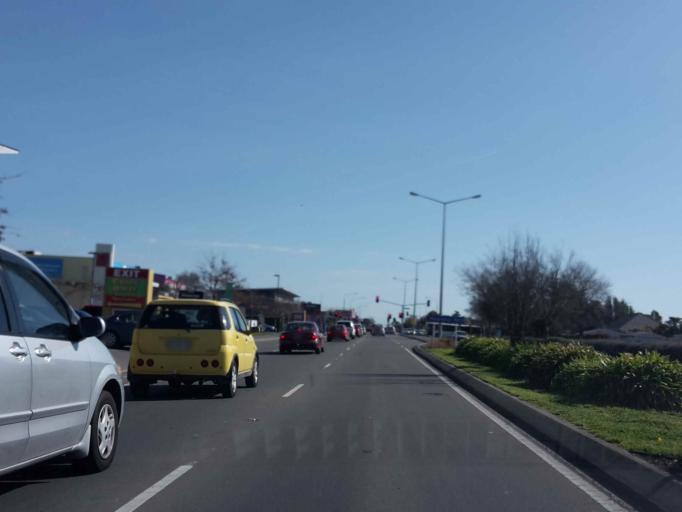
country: NZ
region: Canterbury
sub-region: Christchurch City
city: Christchurch
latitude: -43.5381
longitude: 172.5895
